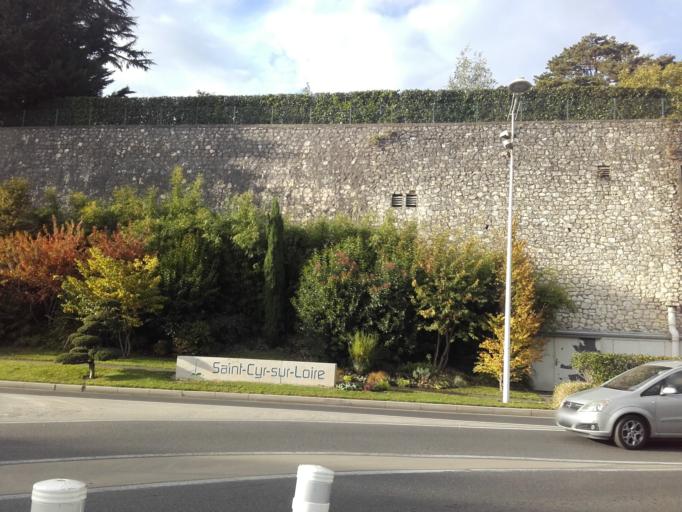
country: FR
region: Centre
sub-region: Departement d'Indre-et-Loire
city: Saint-Cyr-sur-Loire
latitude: 47.4007
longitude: 0.6751
